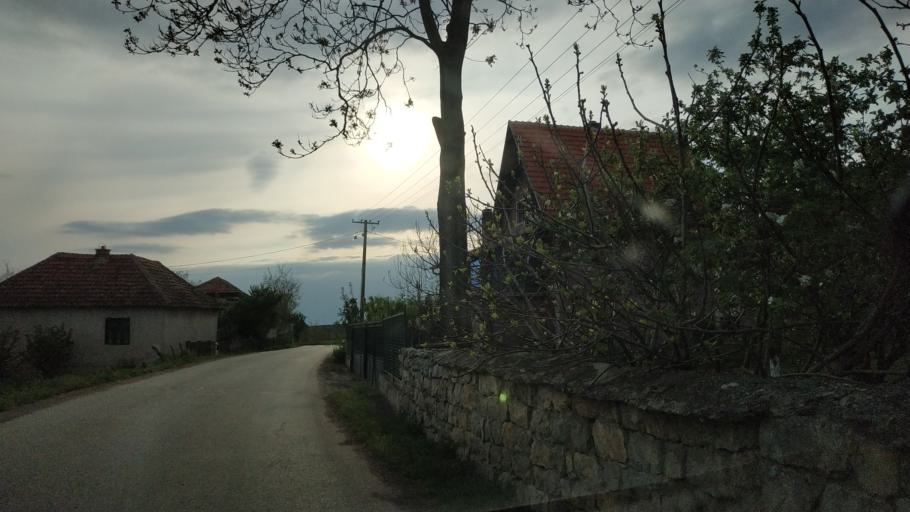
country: RS
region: Central Serbia
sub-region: Zajecarski Okrug
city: Soko Banja
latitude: 43.5256
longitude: 21.8507
